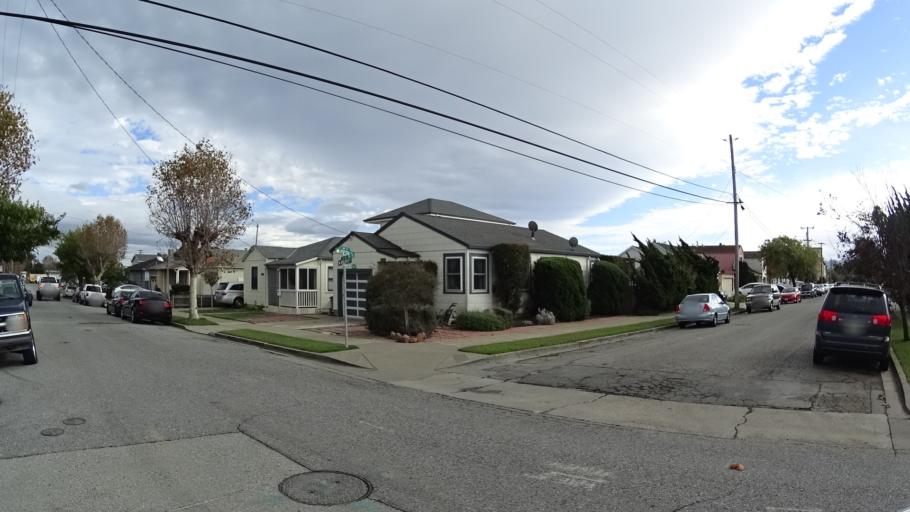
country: US
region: California
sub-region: San Mateo County
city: San Bruno
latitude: 37.6327
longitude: -122.4078
